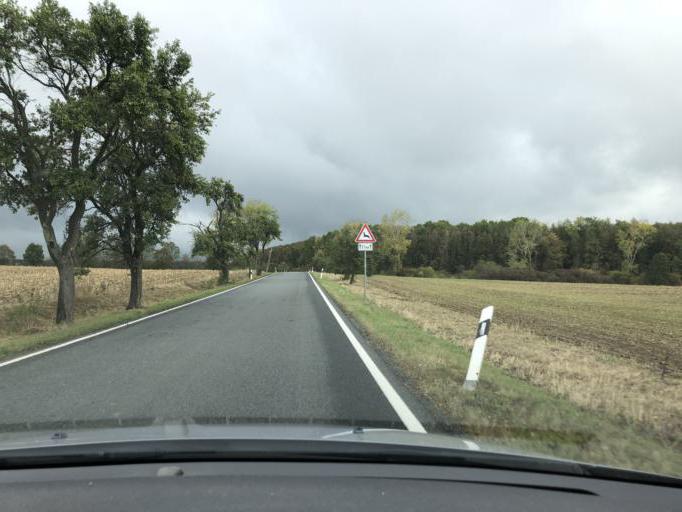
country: DE
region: Thuringia
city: Anrode
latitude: 51.2660
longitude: 10.3539
